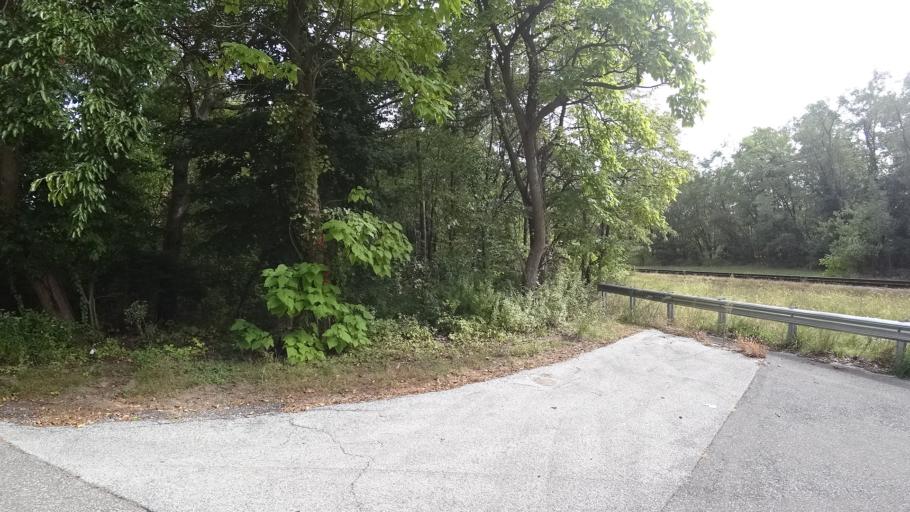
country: US
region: Indiana
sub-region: LaPorte County
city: Michigan City
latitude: 41.7135
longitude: -86.8803
